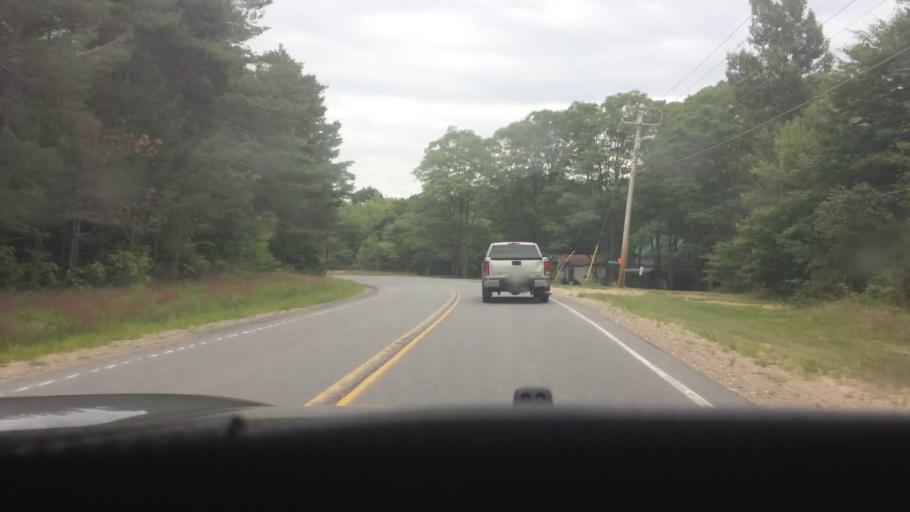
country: US
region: New York
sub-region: St. Lawrence County
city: Canton
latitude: 44.5175
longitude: -75.1976
